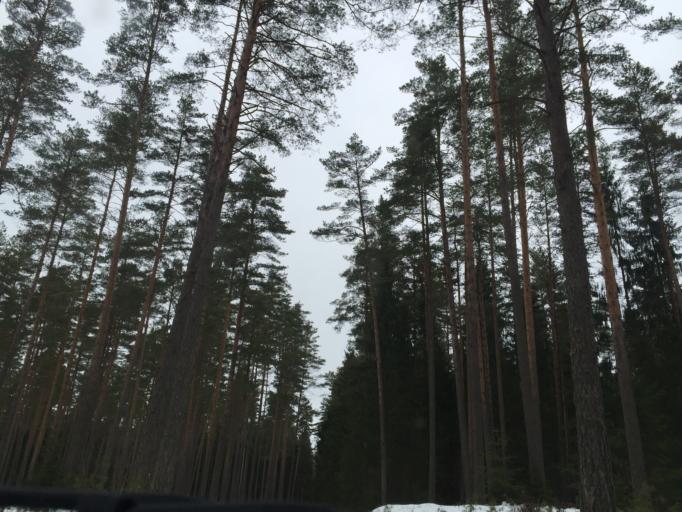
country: LV
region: Krimulda
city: Ragana
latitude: 57.1346
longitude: 24.7399
